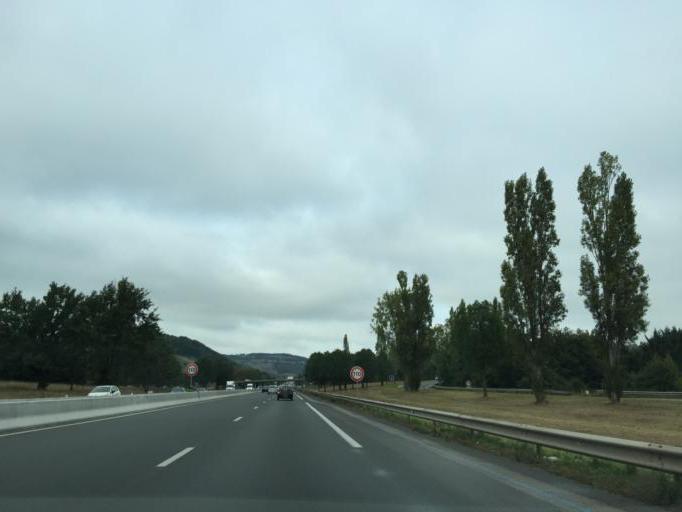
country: FR
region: Rhone-Alpes
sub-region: Departement de la Loire
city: Villars
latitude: 45.4780
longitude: 4.3538
